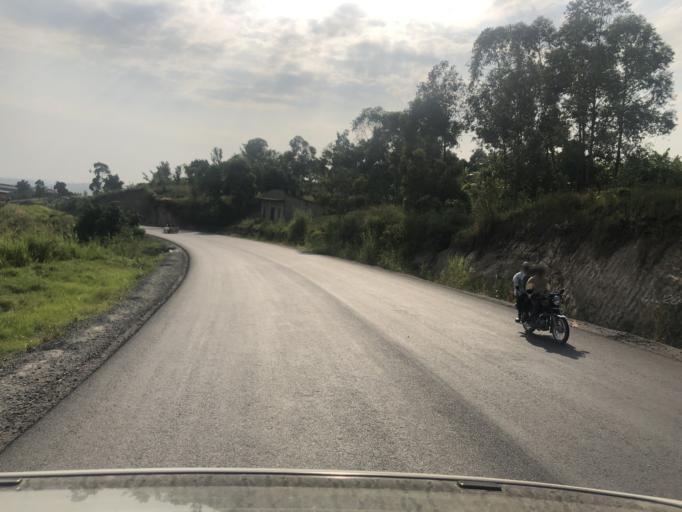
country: UG
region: Western Region
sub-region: Rubirizi District
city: Rubirizi
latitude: -0.2241
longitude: 30.0959
